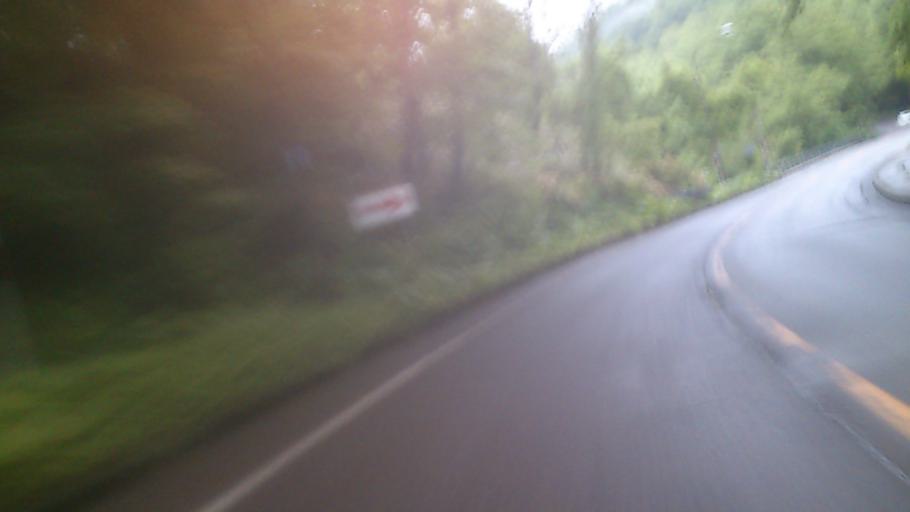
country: JP
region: Hokkaido
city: Shiraoi
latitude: 42.7676
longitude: 141.4147
